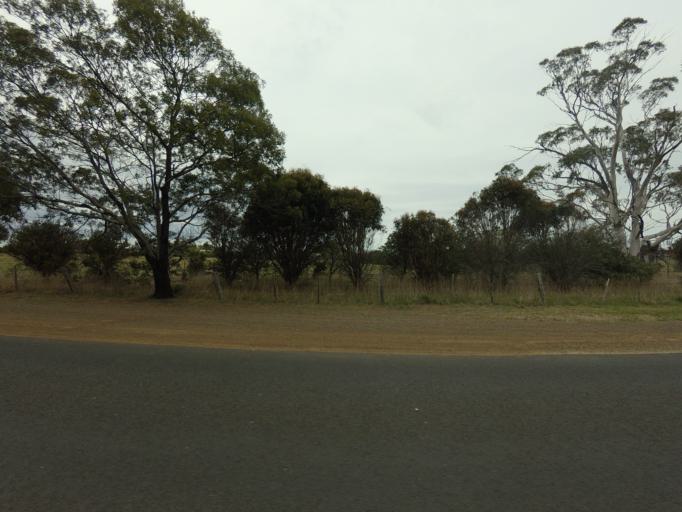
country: AU
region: Tasmania
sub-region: Sorell
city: Sorell
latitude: -42.1347
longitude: 148.0712
